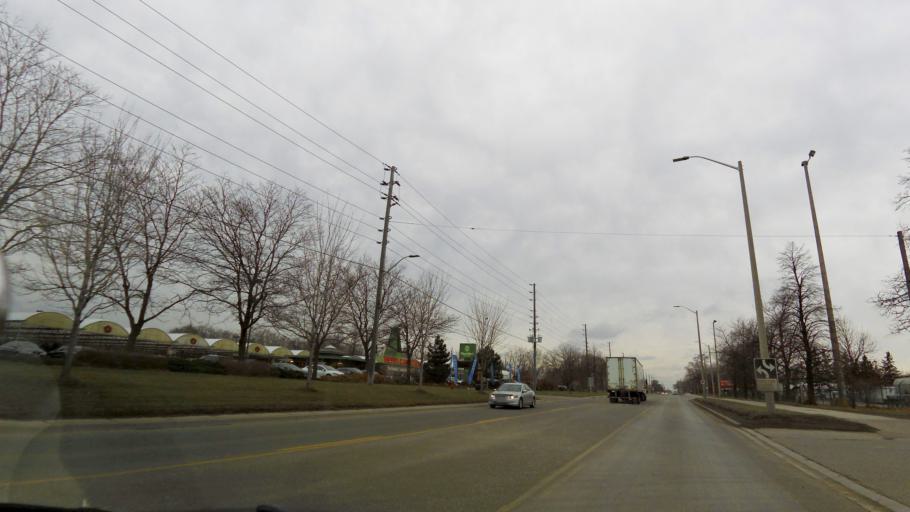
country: CA
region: Ontario
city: Oakville
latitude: 43.5031
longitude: -79.6193
